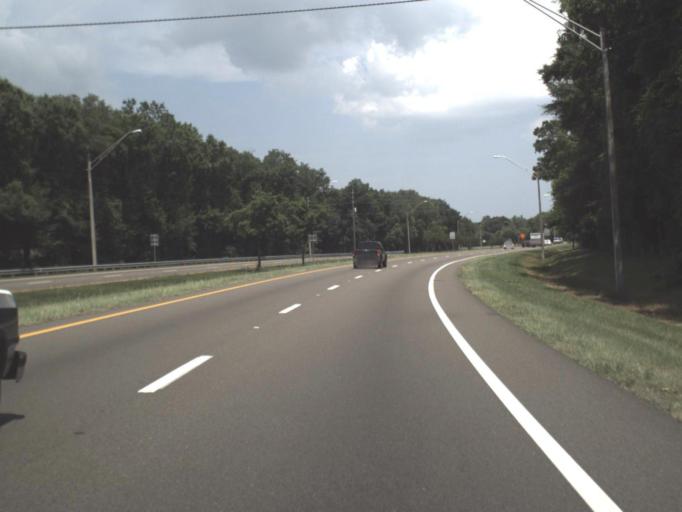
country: US
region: Florida
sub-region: Duval County
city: Jacksonville
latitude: 30.3568
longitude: -81.6849
